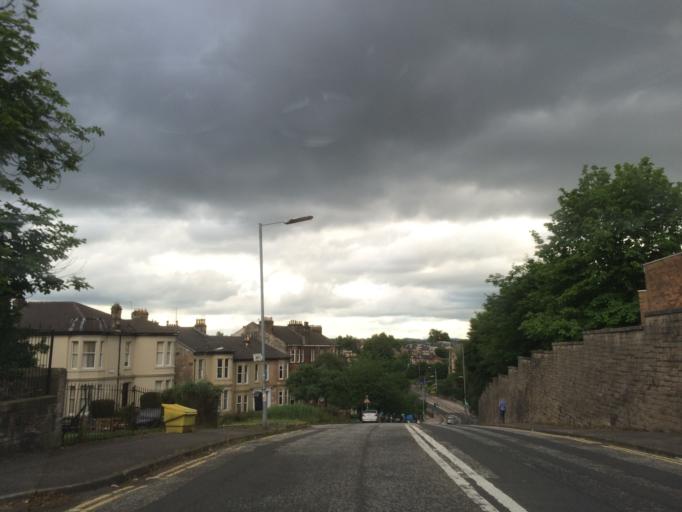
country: GB
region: Scotland
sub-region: East Renfrewshire
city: Giffnock
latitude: 55.8238
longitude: -4.2757
